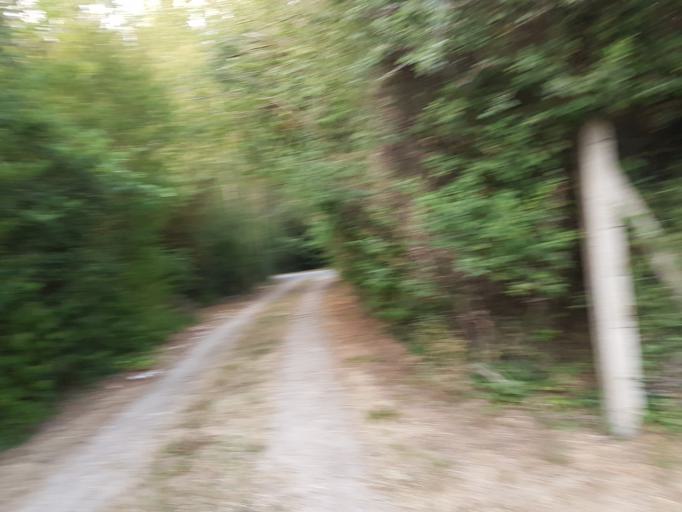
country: FR
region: Centre
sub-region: Departement d'Indre-et-Loire
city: Saint-Avertin
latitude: 47.3552
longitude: 0.7579
